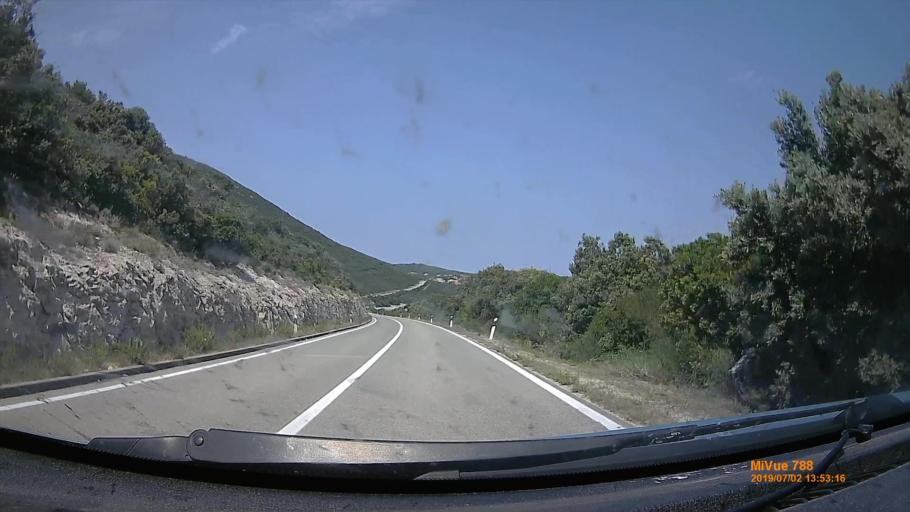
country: HR
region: Primorsko-Goranska
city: Mali Losinj
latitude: 44.6241
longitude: 14.3936
